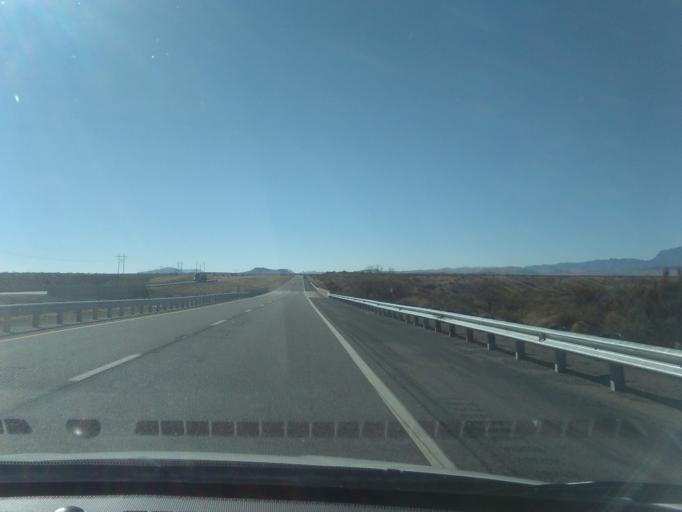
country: US
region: New Mexico
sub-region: Sierra County
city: Elephant Butte
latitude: 33.6199
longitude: -107.1408
